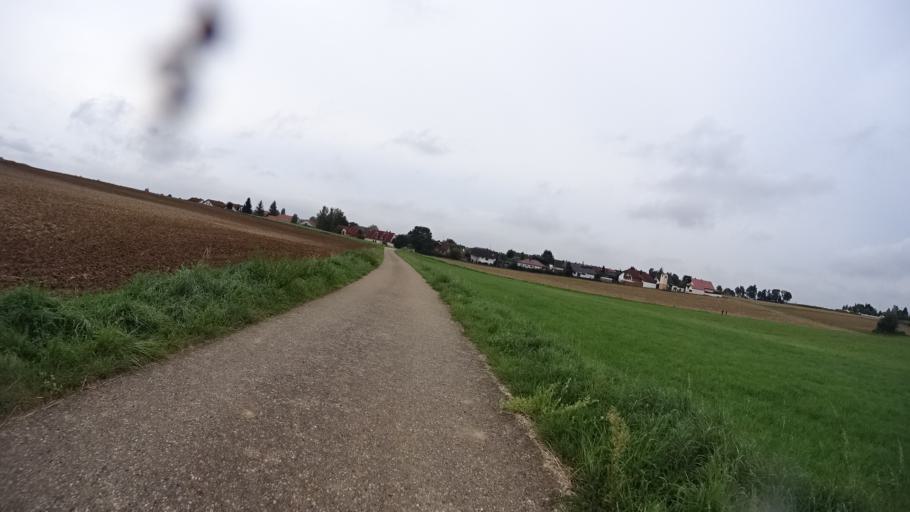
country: DE
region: Bavaria
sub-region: Upper Bavaria
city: Bohmfeld
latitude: 48.8404
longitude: 11.3552
